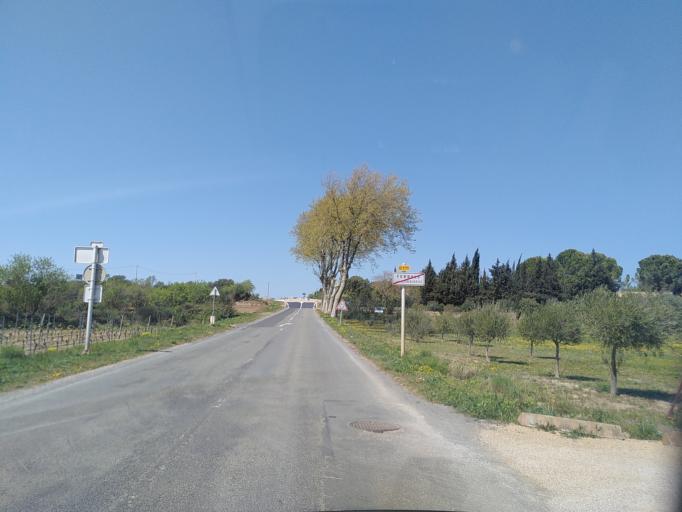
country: FR
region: Languedoc-Roussillon
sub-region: Departement de l'Aude
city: Ferrals-les-Corbieres
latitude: 43.1522
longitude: 2.7180
